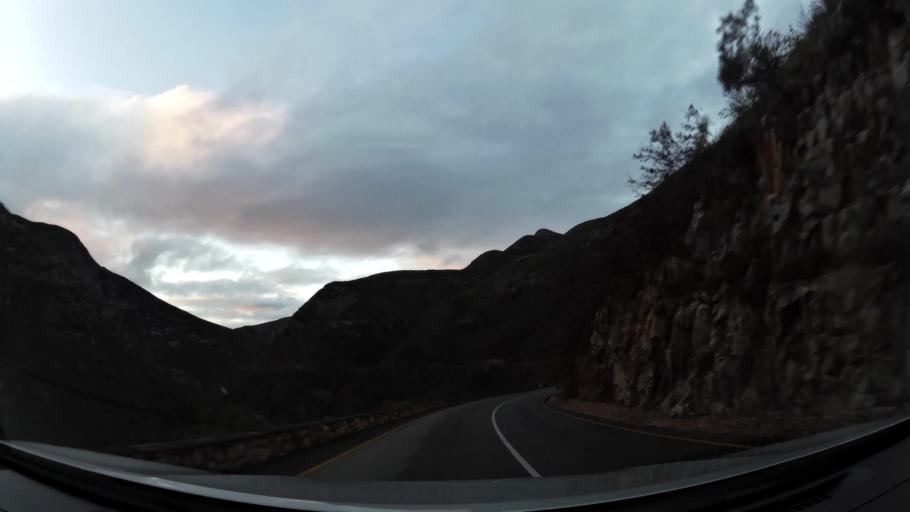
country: ZA
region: Western Cape
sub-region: Overberg District Municipality
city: Swellendam
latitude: -33.9699
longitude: 20.7017
